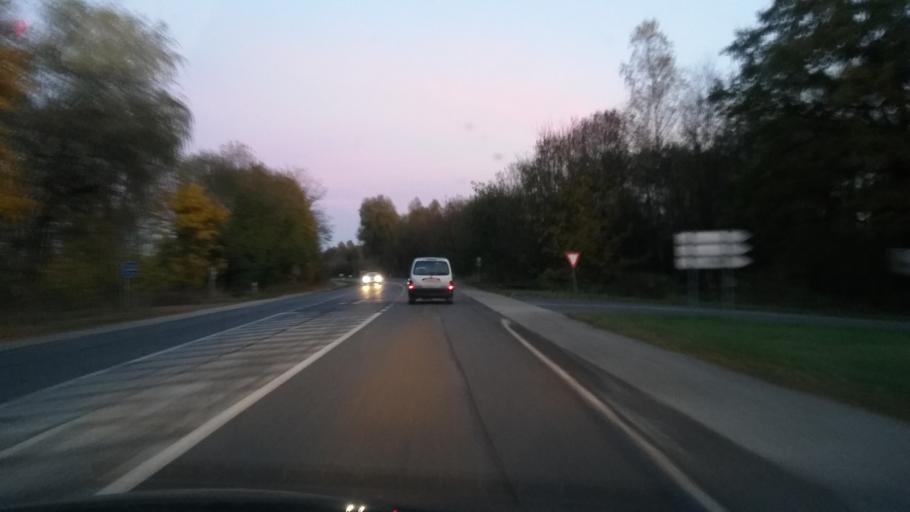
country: BE
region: Wallonia
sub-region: Province du Luxembourg
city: Etalle
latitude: 49.6723
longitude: 5.5806
